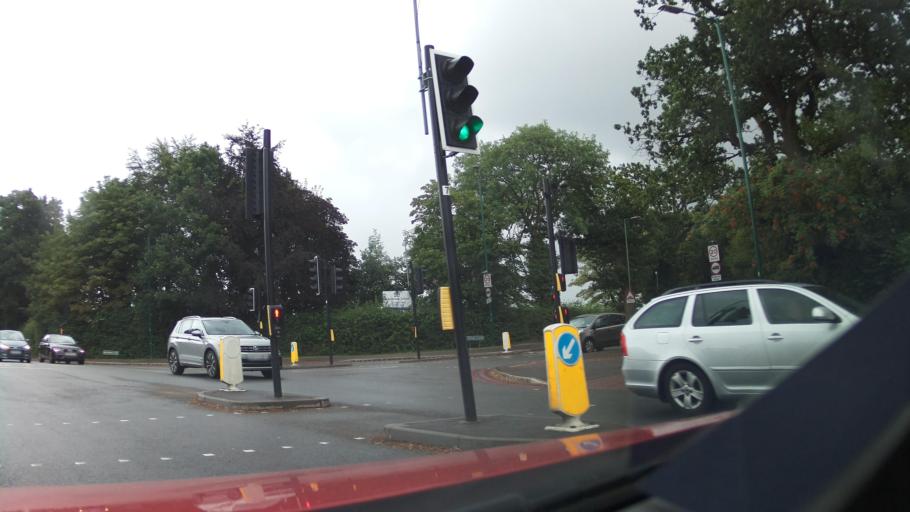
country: GB
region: England
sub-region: Solihull
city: Shirley
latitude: 52.4061
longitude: -1.8010
